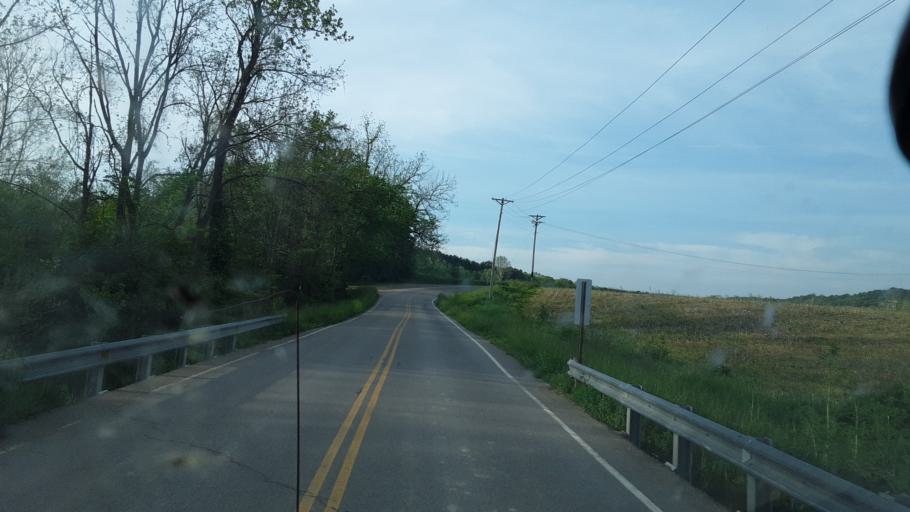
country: US
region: Ohio
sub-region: Ross County
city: Kingston
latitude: 39.5106
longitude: -82.6991
